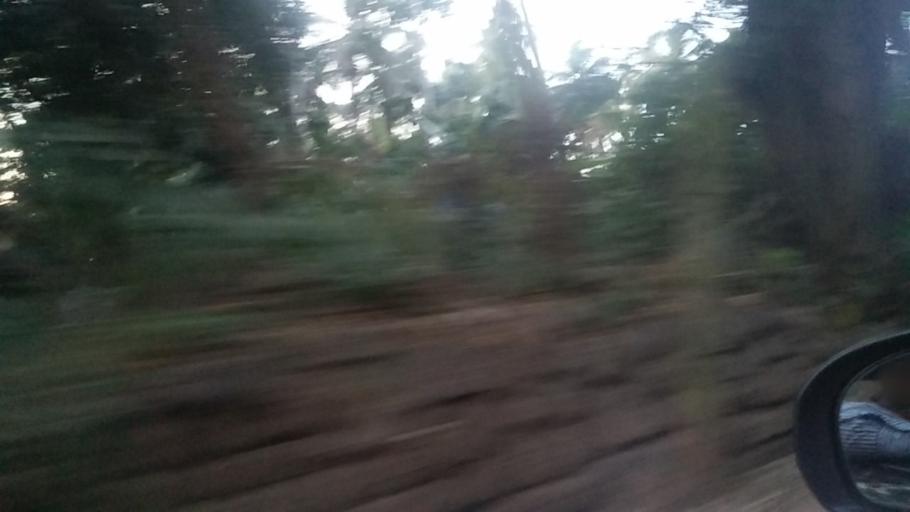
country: IN
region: Goa
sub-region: North Goa
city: Bambolim
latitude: 15.4681
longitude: 73.8467
